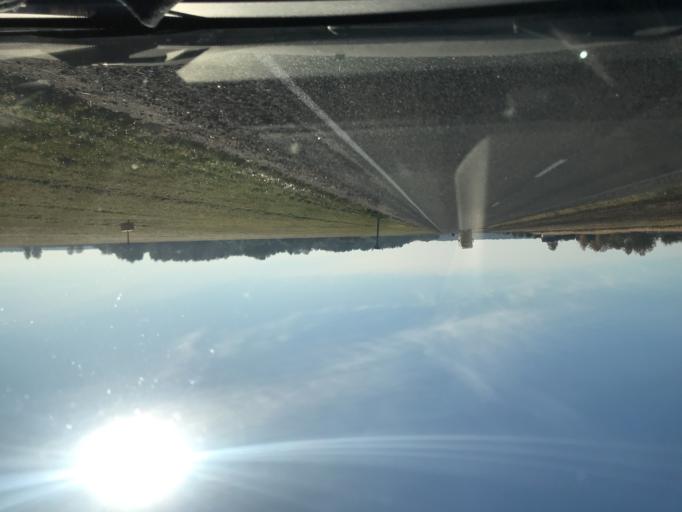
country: BY
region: Gomel
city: Brahin
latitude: 51.7744
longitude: 30.2624
